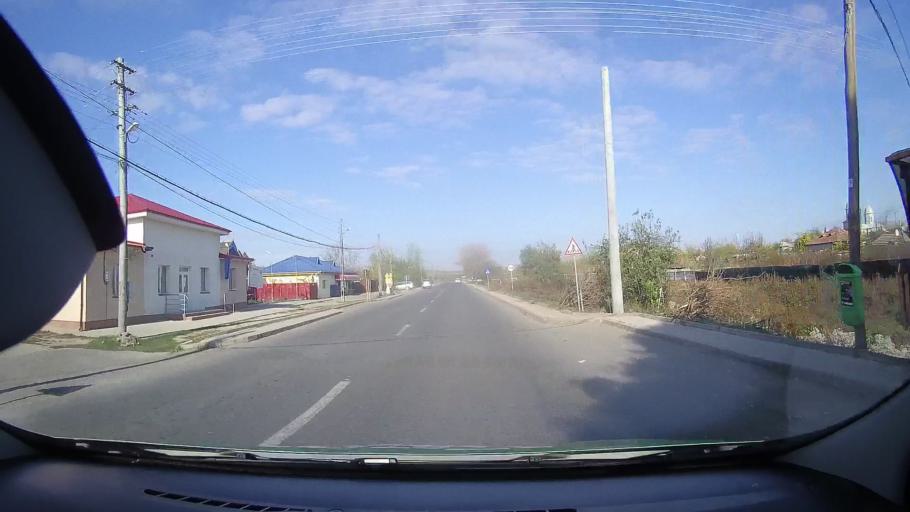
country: RO
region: Tulcea
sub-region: Comuna Valea Nucarilor
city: Valea Nucarilor
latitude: 45.0408
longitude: 28.9363
